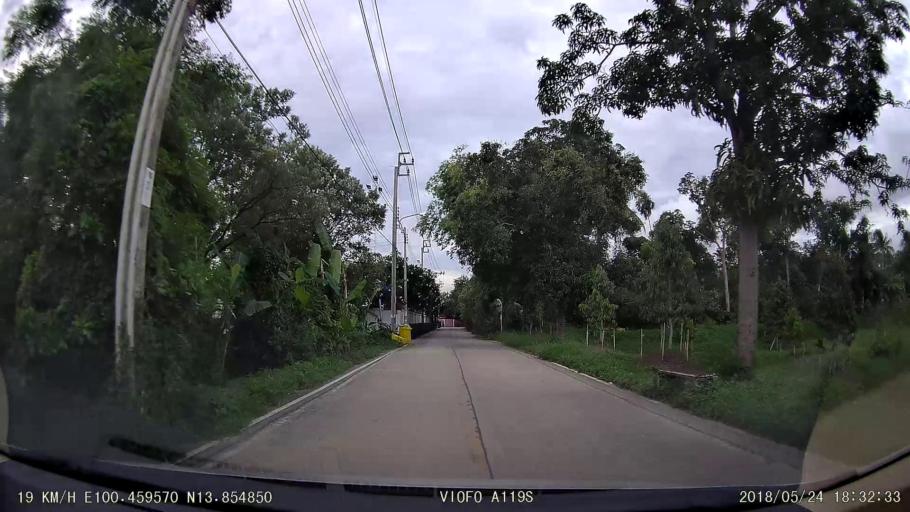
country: TH
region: Nonthaburi
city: Bang Kruai
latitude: 13.8542
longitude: 100.4591
